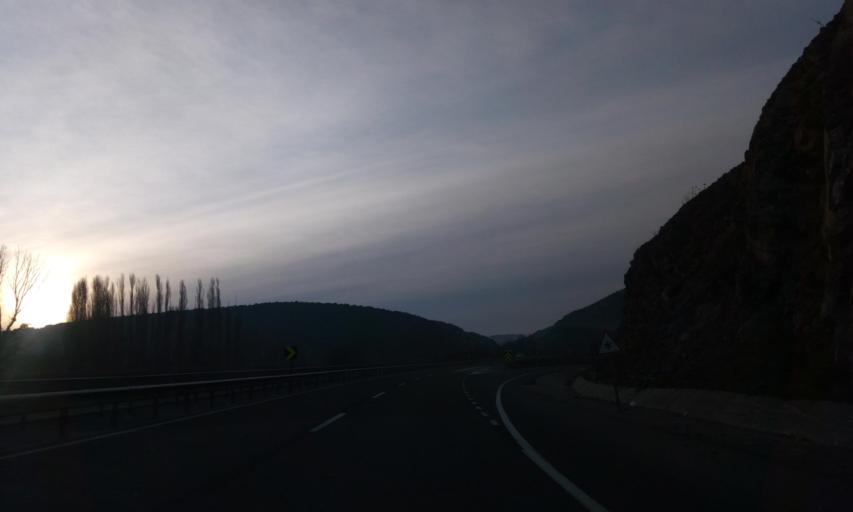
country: TR
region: Bilecik
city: Bilecik
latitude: 40.1478
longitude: 30.0259
